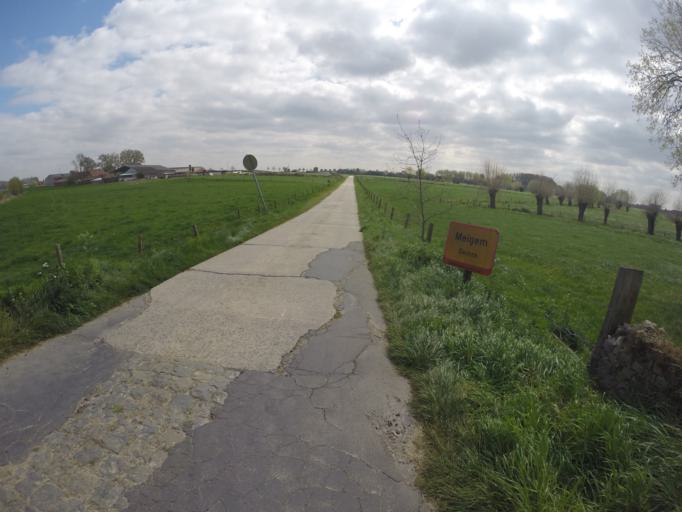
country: BE
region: Flanders
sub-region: Provincie Oost-Vlaanderen
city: Nevele
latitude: 51.0255
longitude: 3.4922
